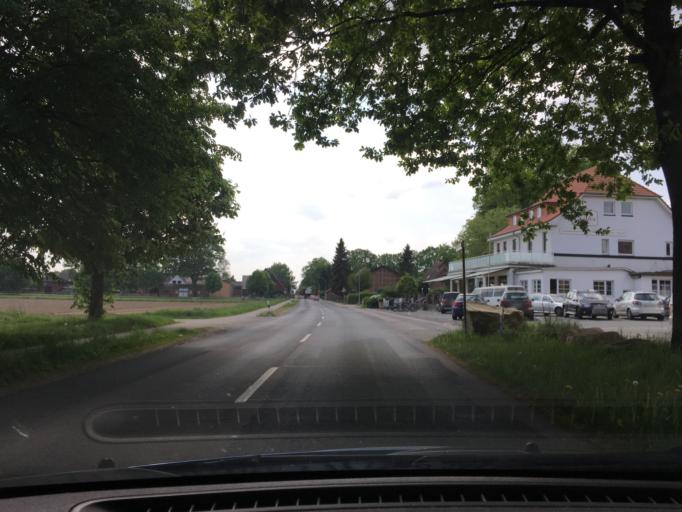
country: DE
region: Lower Saxony
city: Seevetal
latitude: 53.4243
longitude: 9.8981
